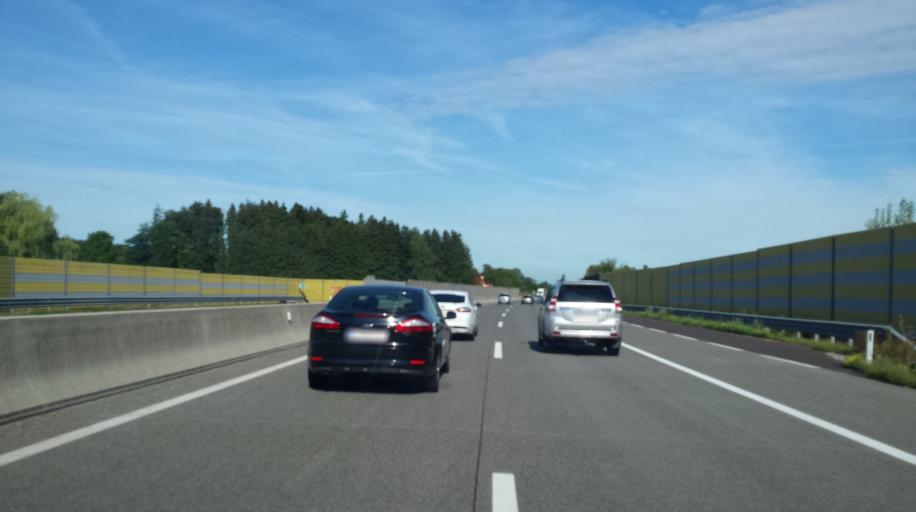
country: AT
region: Upper Austria
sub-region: Politischer Bezirk Vocklabruck
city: Aurach am Hongar
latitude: 47.9494
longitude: 13.6708
